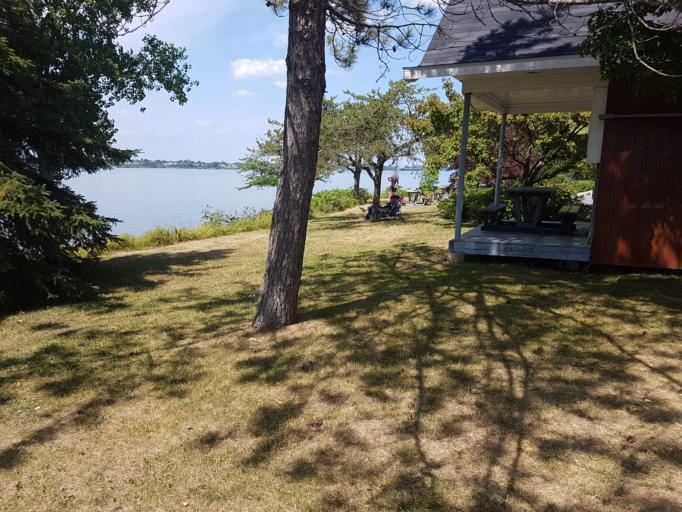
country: CA
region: Quebec
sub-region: Mauricie
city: Trois-Rivieres
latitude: 46.3413
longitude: -72.5009
